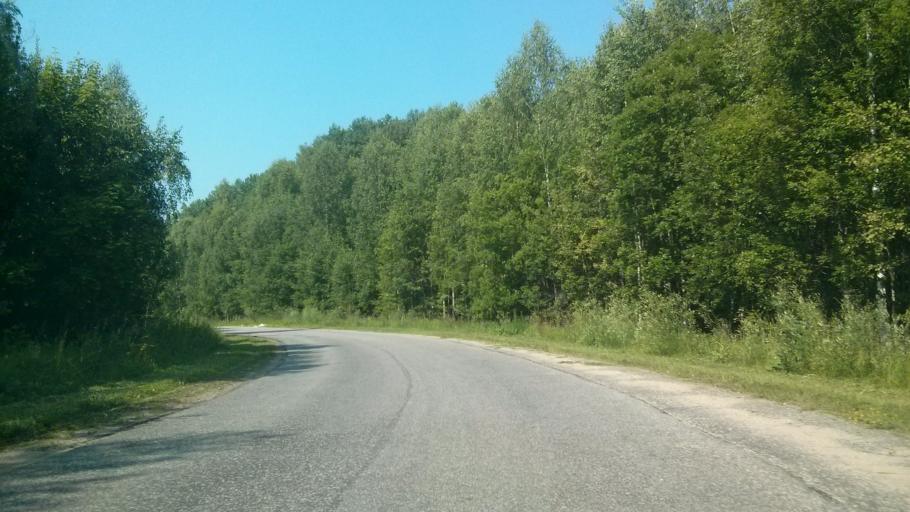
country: RU
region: Vladimir
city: Murom
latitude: 55.5066
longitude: 41.9907
